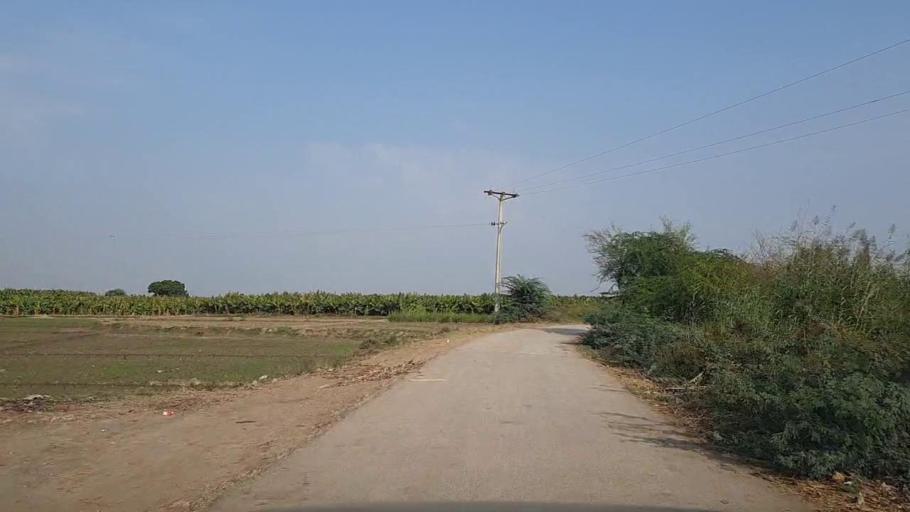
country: PK
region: Sindh
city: Thatta
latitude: 24.6460
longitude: 67.9351
